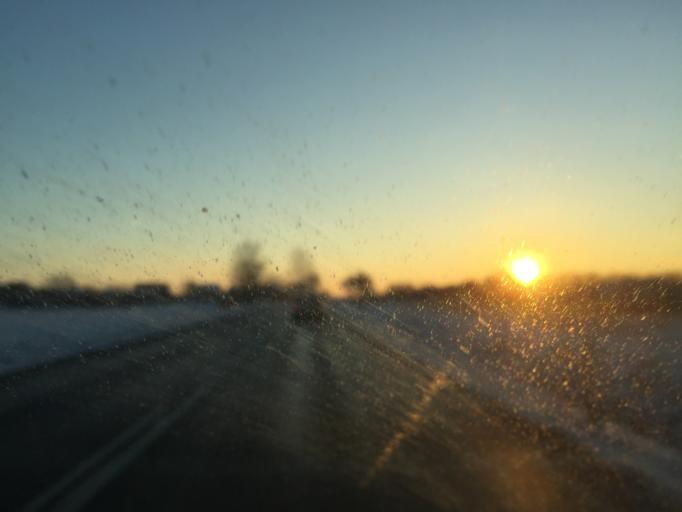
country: PL
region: Kujawsko-Pomorskie
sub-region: Powiat torunski
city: Lubicz Dolny
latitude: 53.0737
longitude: 18.7611
